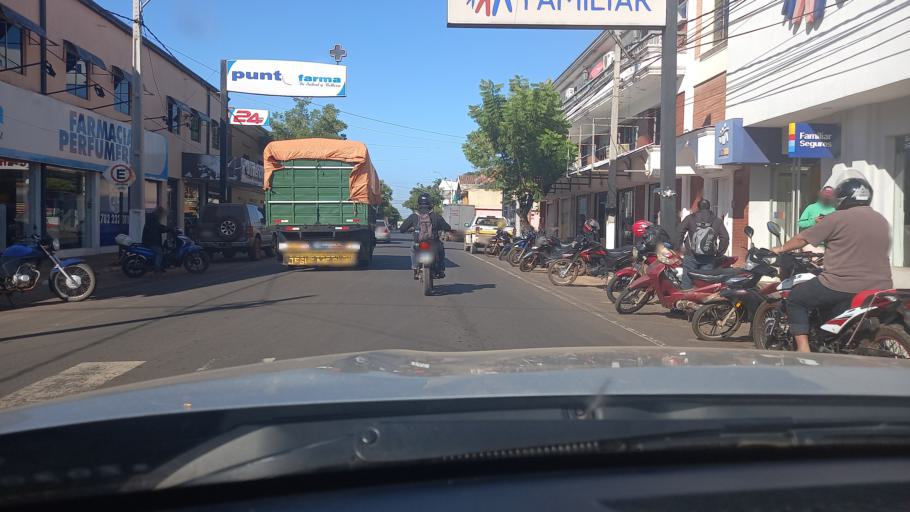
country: PY
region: Misiones
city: Santa Maria
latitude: -26.8875
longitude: -57.0229
